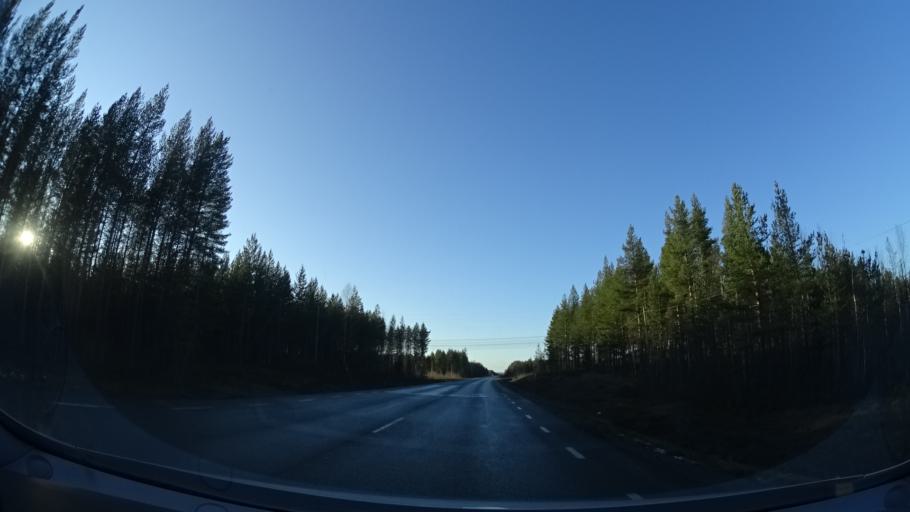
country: SE
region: Vaesterbotten
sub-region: Norsjo Kommun
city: Norsjoe
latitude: 64.9765
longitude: 19.6606
